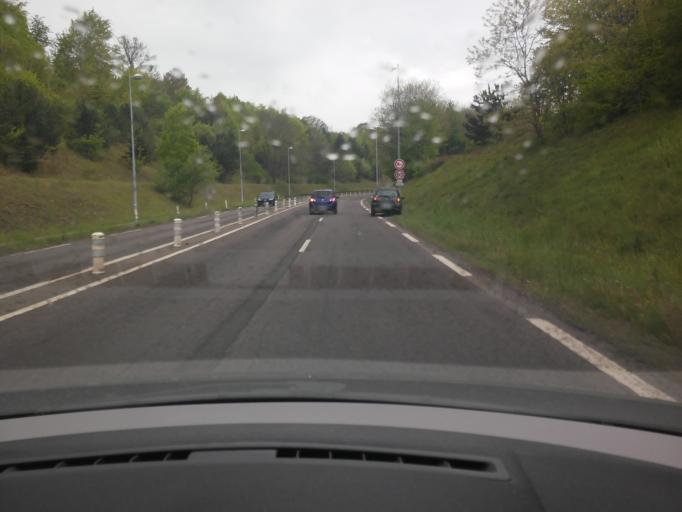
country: FR
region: Lorraine
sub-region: Departement de Meurthe-et-Moselle
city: Laxou
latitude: 48.6848
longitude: 6.1384
